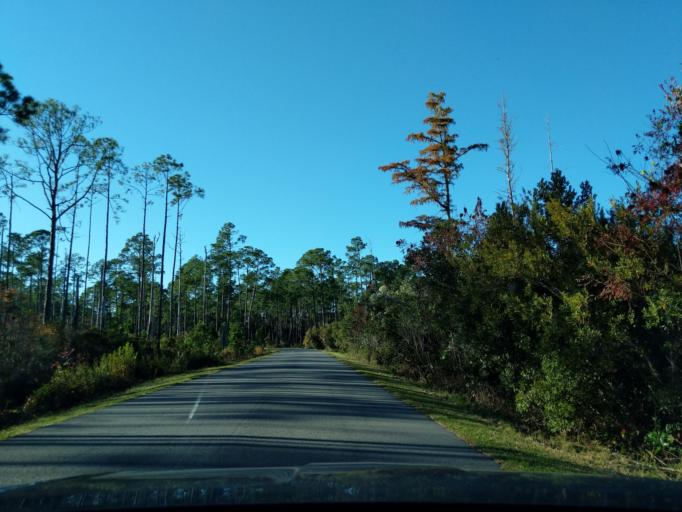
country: US
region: Georgia
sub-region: Charlton County
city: Folkston
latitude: 30.7110
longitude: -82.1529
